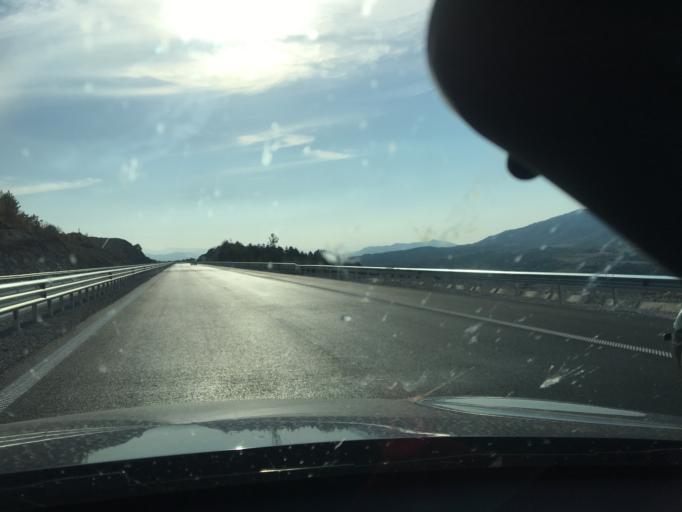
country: BG
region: Lovech
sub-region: Obshtina Yablanitsa
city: Yablanitsa
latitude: 43.0435
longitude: 24.1266
